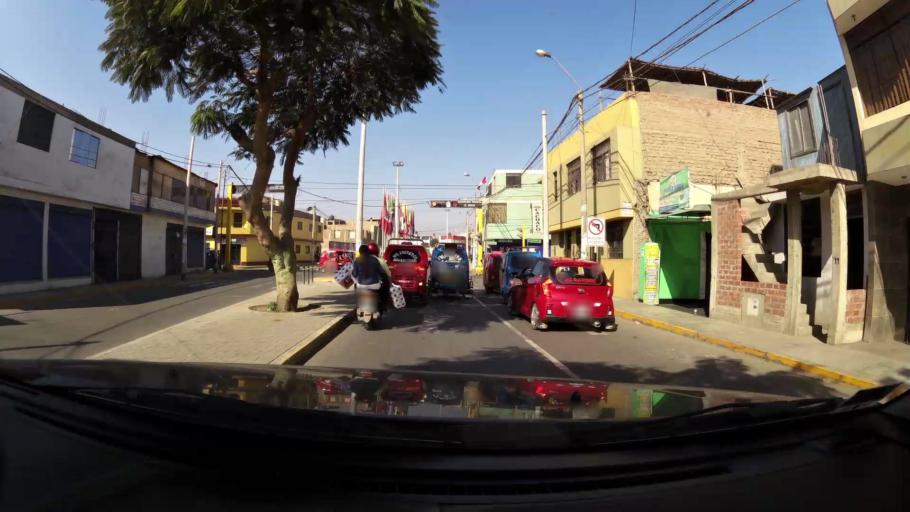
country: PE
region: Ica
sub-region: Provincia de Chincha
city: Chincha Alta
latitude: -13.4215
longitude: -76.1323
